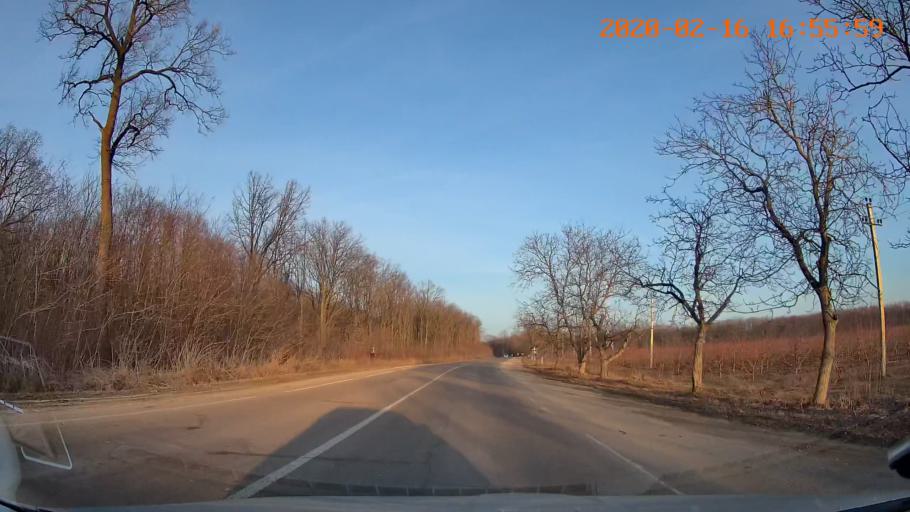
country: MD
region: Briceni
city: Briceni
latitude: 48.3298
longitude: 27.0415
